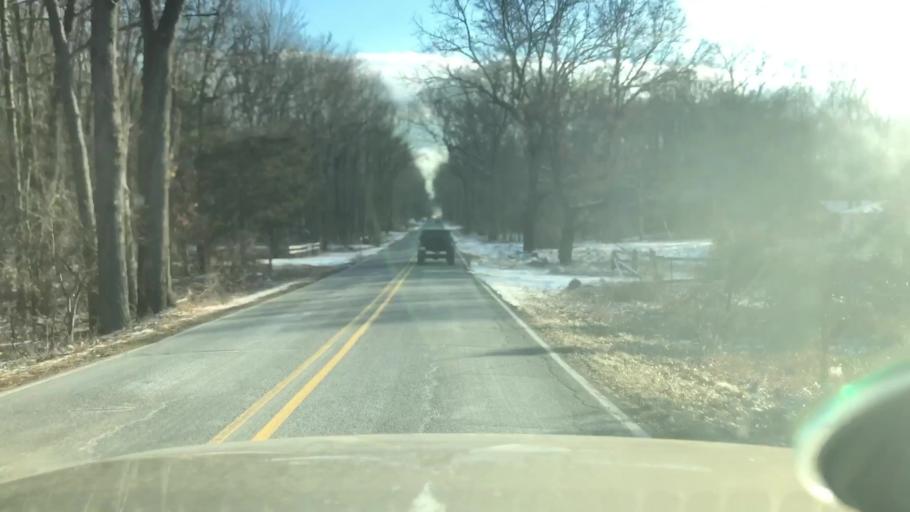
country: US
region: Michigan
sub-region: Jackson County
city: Vandercook Lake
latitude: 42.1137
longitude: -84.4513
